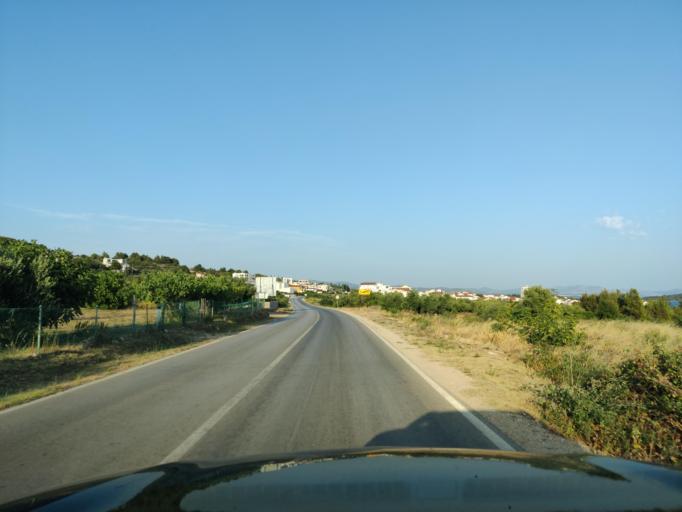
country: HR
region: Sibensko-Kniniska
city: Tribunj
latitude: 43.7589
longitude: 15.7549
